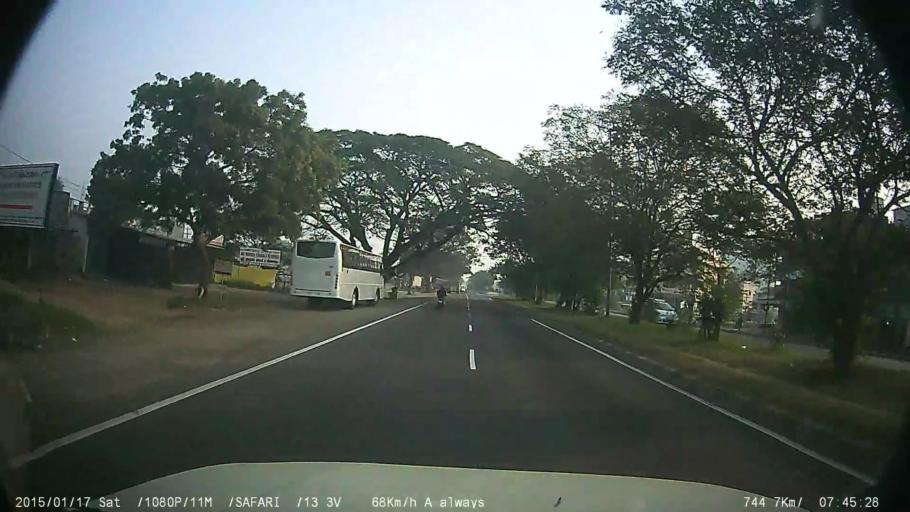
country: IN
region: Tamil Nadu
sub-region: Kancheepuram
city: Guduvancheri
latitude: 12.8296
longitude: 80.0445
